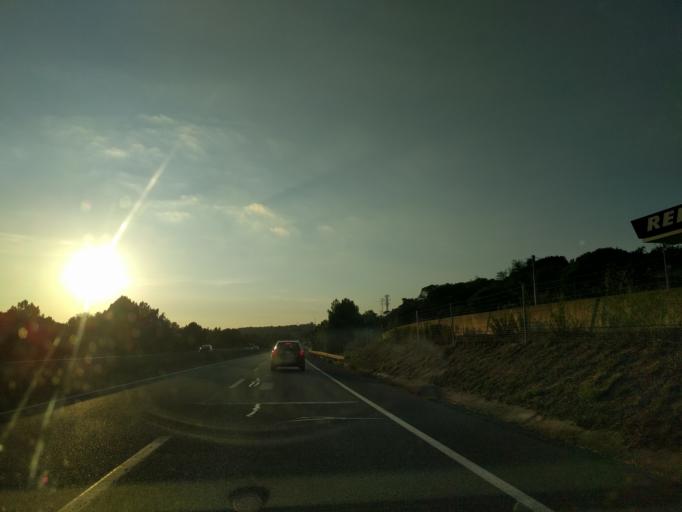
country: ES
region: Catalonia
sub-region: Provincia de Girona
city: Llagostera
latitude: 41.8272
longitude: 2.9468
